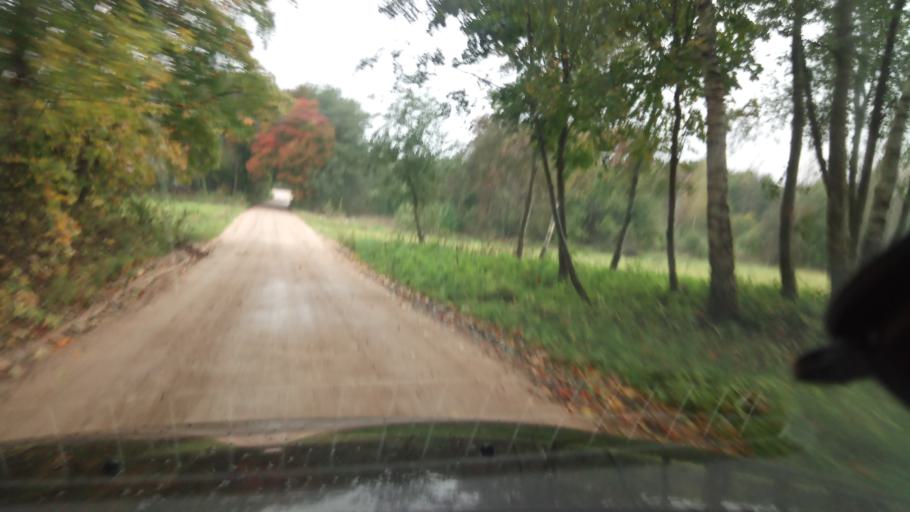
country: LT
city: Skaidiskes
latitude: 54.5569
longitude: 25.4903
